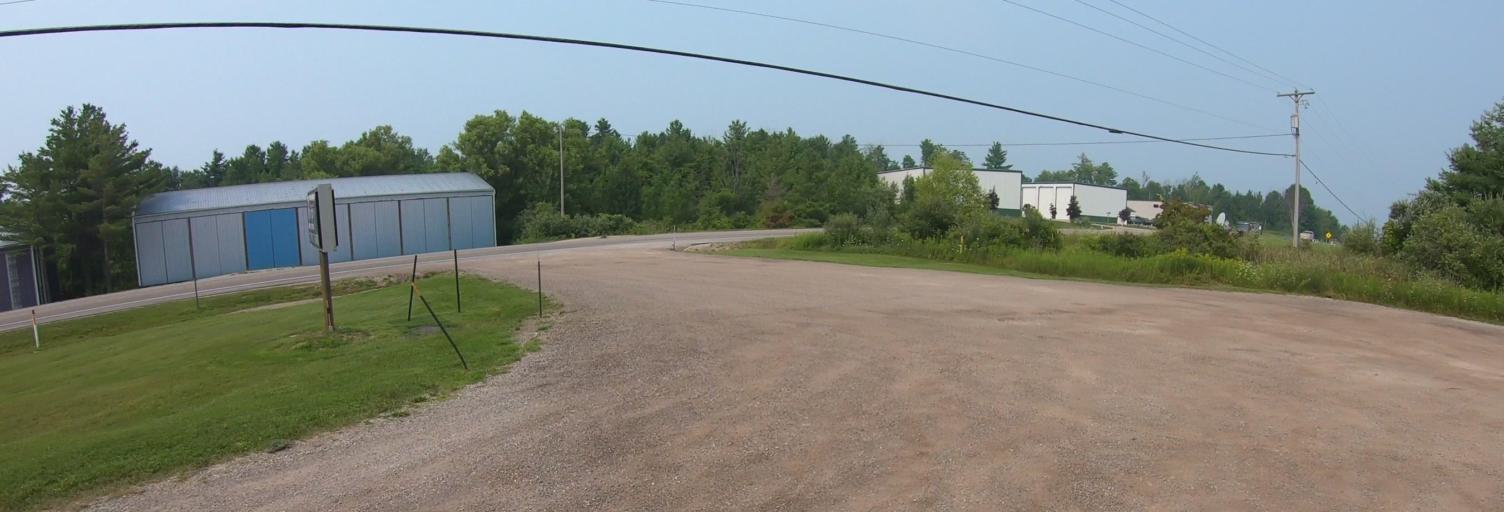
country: US
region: Michigan
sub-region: Antrim County
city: Elk Rapids
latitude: 44.8837
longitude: -85.4187
